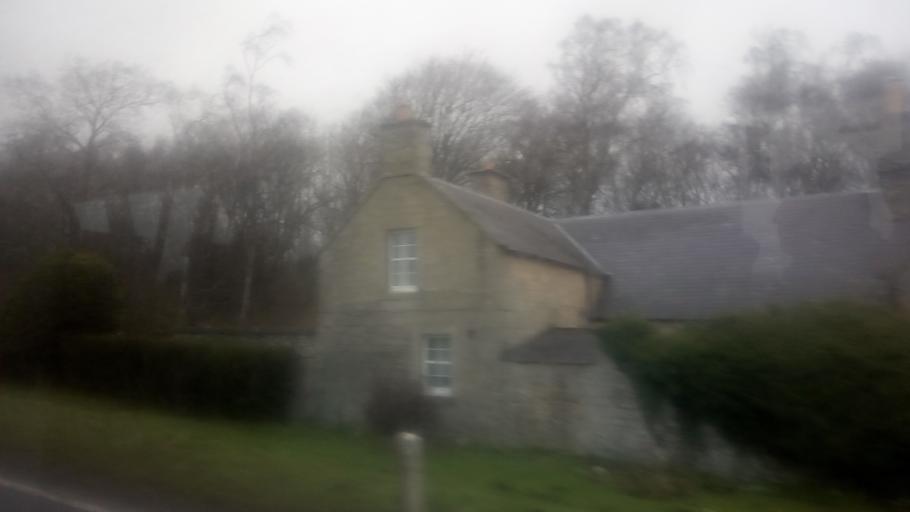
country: GB
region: Scotland
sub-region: The Scottish Borders
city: Saint Boswells
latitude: 55.5615
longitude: -2.6461
